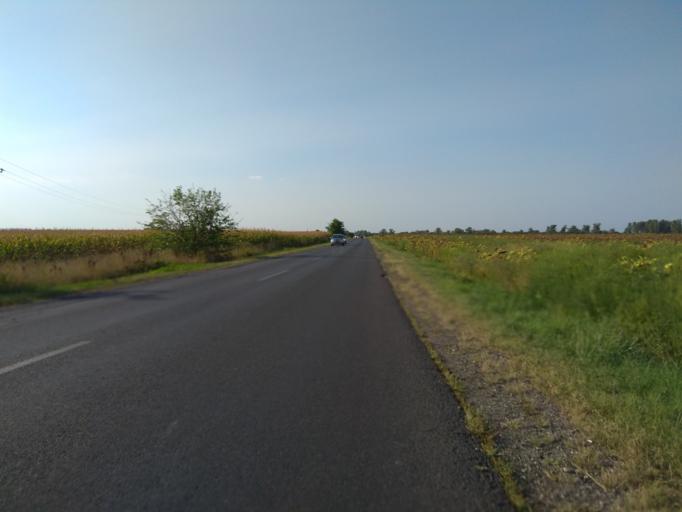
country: HU
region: Borsod-Abauj-Zemplen
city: Onod
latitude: 48.0166
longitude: 20.9066
